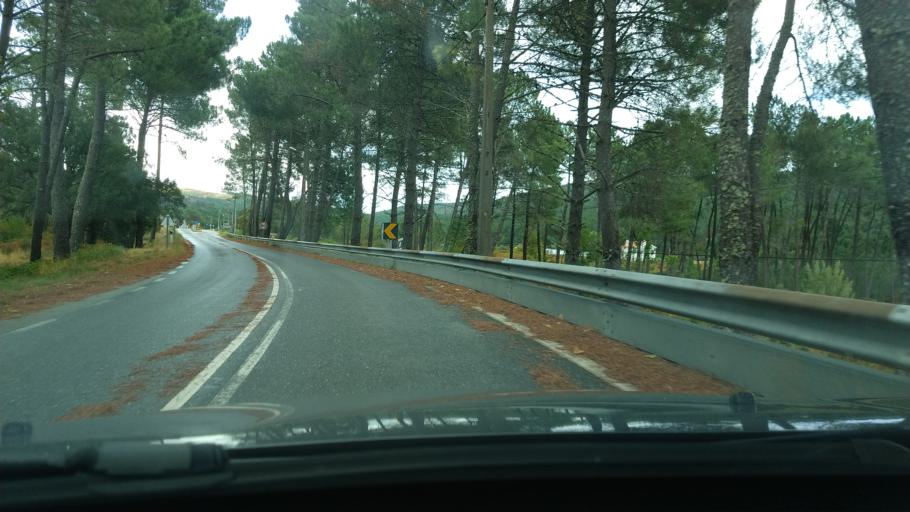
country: PT
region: Castelo Branco
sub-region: Covilha
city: Covilha
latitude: 40.2377
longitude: -7.5910
